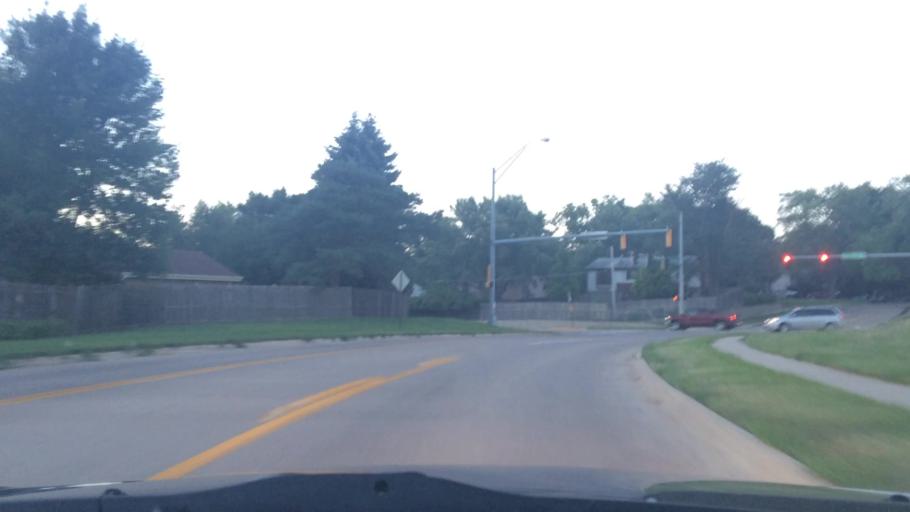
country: US
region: Nebraska
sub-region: Douglas County
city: Ralston
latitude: 41.1914
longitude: -96.0521
